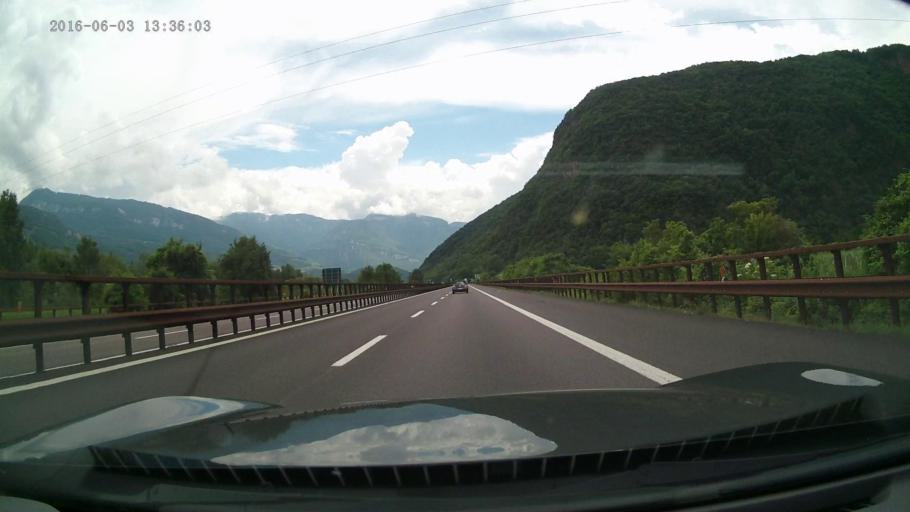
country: IT
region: Trentino-Alto Adige
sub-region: Bolzano
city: Ora
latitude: 46.3784
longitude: 11.2913
